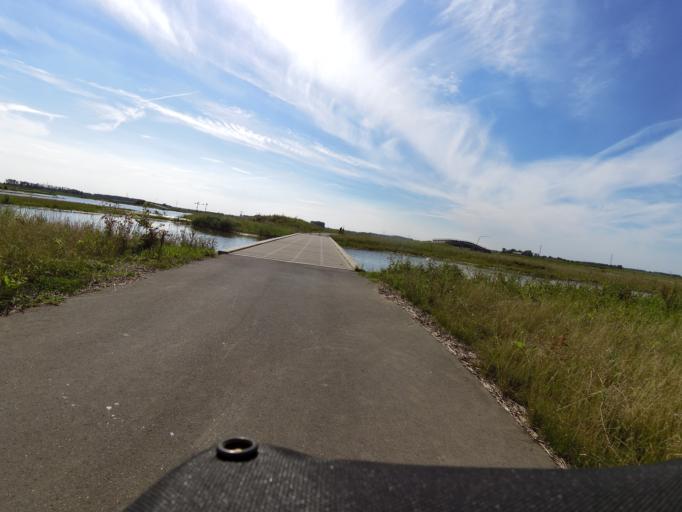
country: NL
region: North Brabant
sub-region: Gemeente Werkendam
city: Werkendam
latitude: 51.7877
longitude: 4.8615
